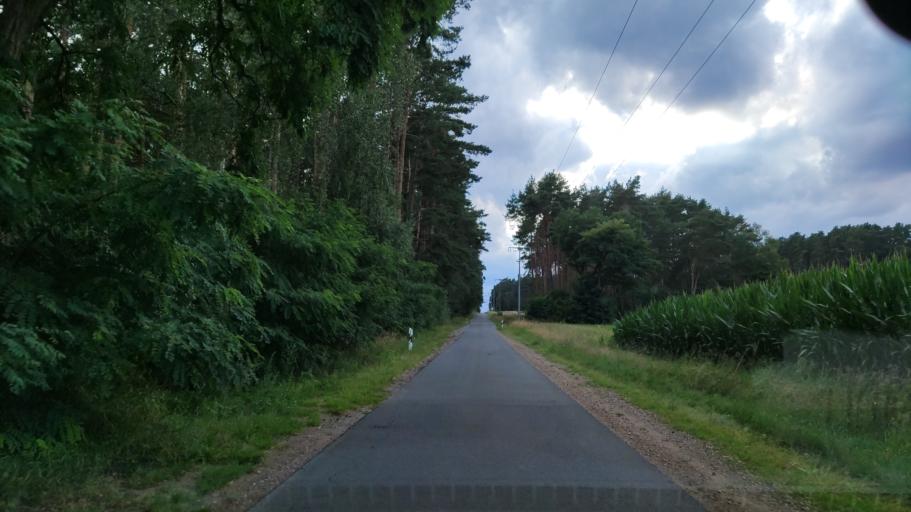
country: DE
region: Lower Saxony
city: Hitzacker
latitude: 53.1297
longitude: 11.0400
